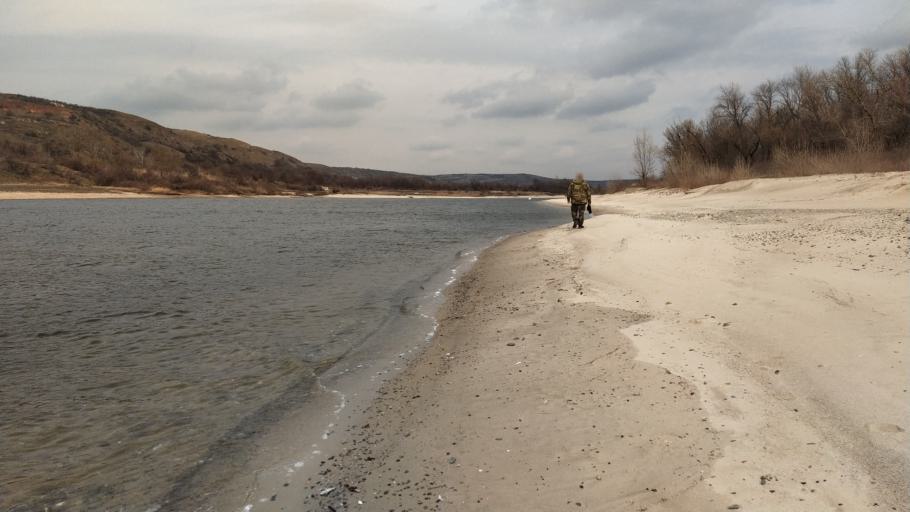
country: RU
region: Rostov
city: Semikarakorsk
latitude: 47.5589
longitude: 40.6731
